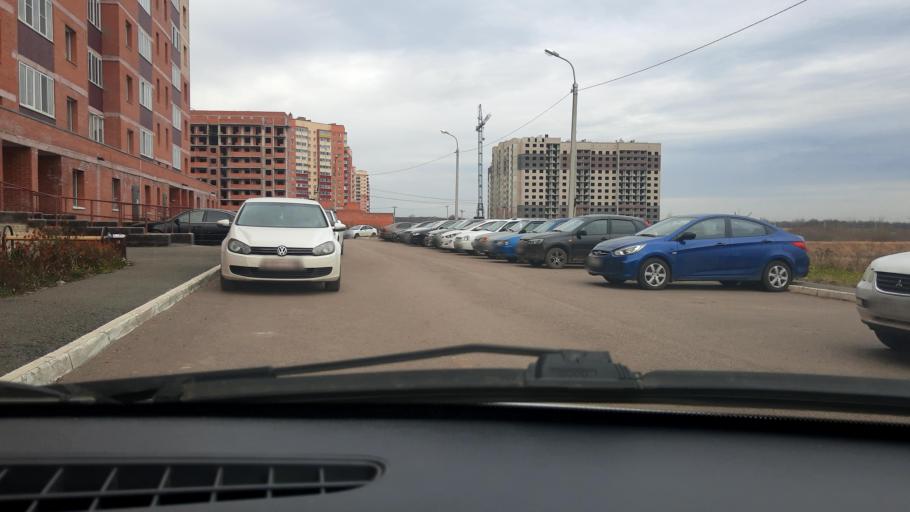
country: RU
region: Bashkortostan
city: Mikhaylovka
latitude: 54.7119
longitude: 55.8481
